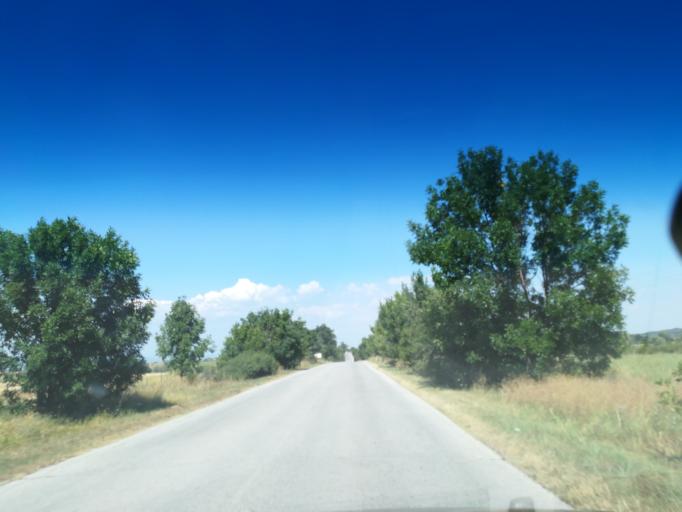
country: BG
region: Plovdiv
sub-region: Obshtina Sadovo
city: Sadovo
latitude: 42.0523
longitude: 25.1486
